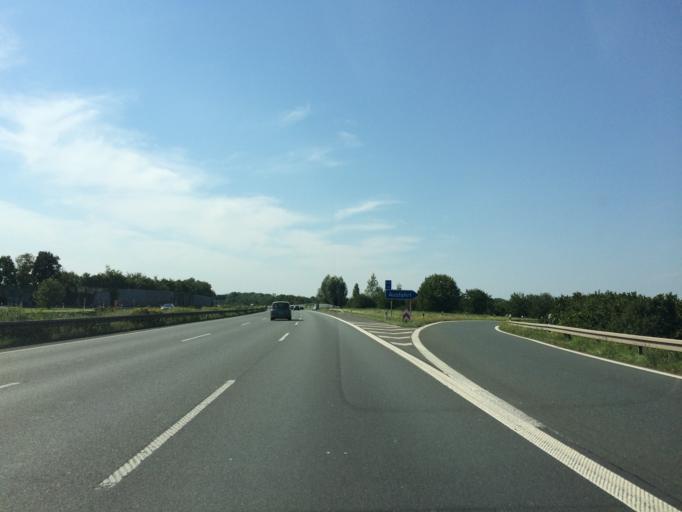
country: DE
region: North Rhine-Westphalia
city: Castrop-Rauxel
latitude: 51.6035
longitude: 7.3207
